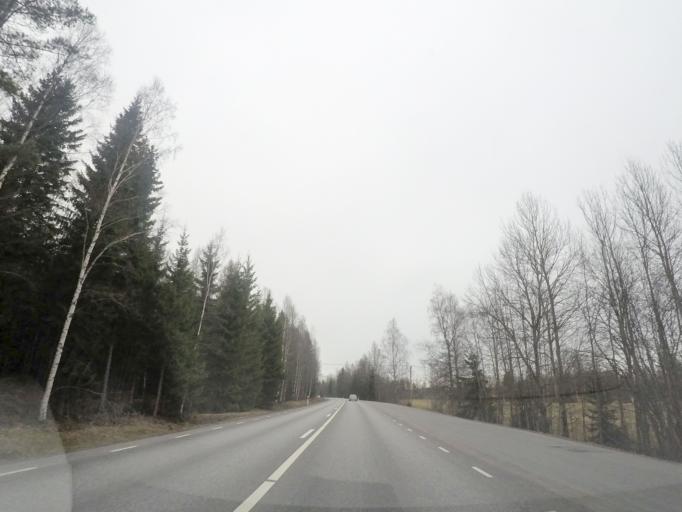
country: SE
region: Vaestmanland
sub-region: Skinnskattebergs Kommun
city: Skinnskatteberg
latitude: 59.8600
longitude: 15.6565
